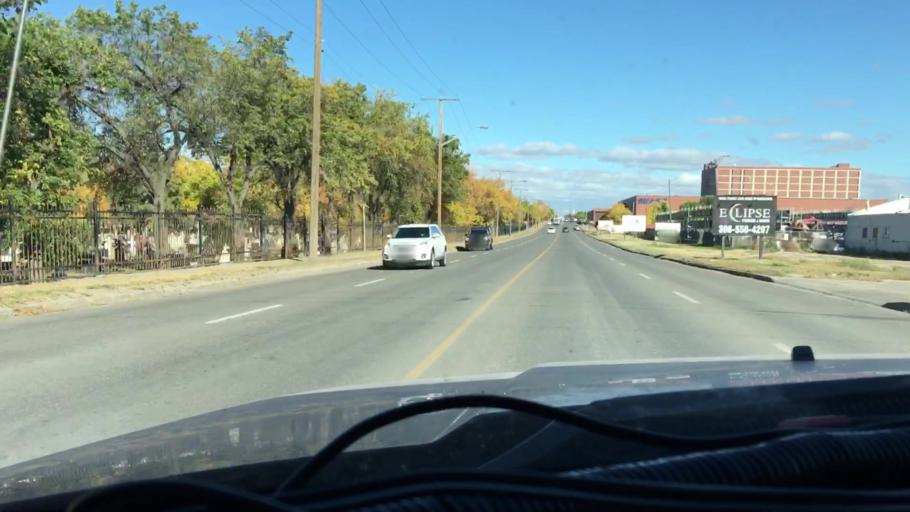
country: CA
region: Saskatchewan
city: Regina
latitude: 50.4629
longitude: -104.6149
